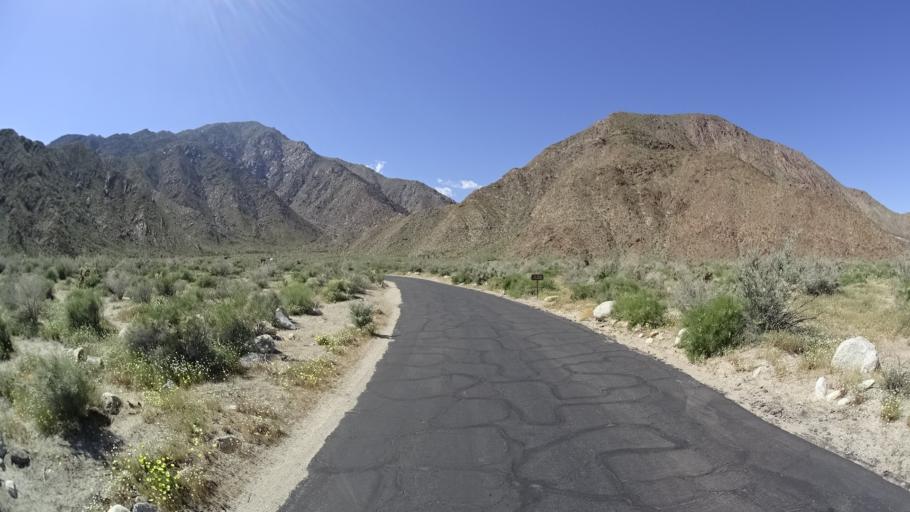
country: US
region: California
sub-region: San Diego County
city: Borrego Springs
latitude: 33.2708
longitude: -116.4140
